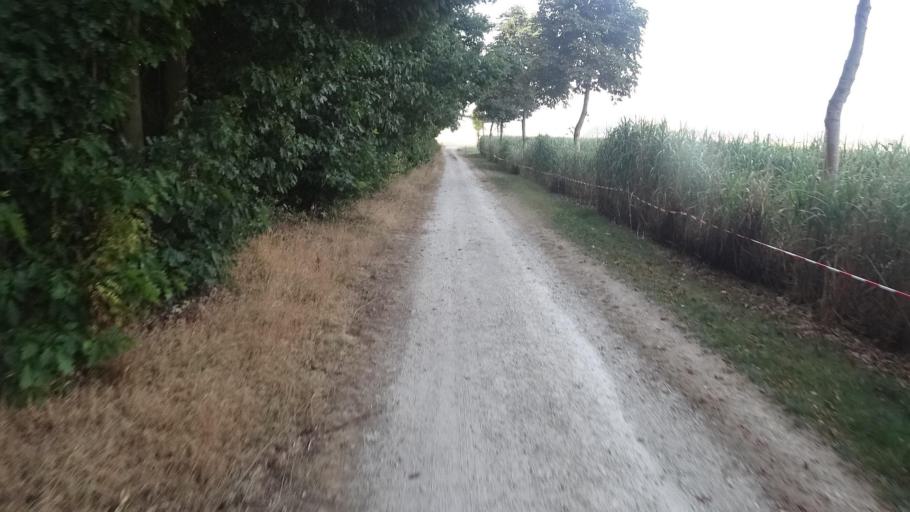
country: DE
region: Rheinland-Pfalz
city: Holzbach
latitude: 49.9457
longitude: 7.5326
